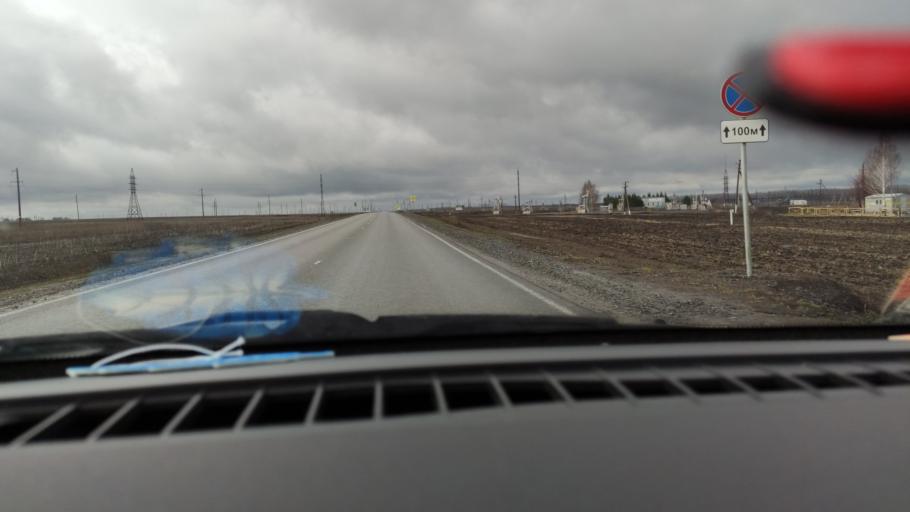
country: RU
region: Tatarstan
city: Nurlat
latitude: 54.4783
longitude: 50.8434
